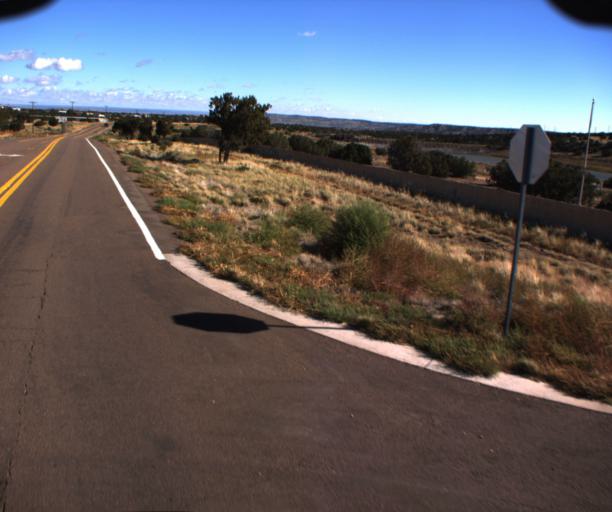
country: US
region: Arizona
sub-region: Apache County
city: Saint Johns
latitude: 34.4466
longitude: -109.6319
